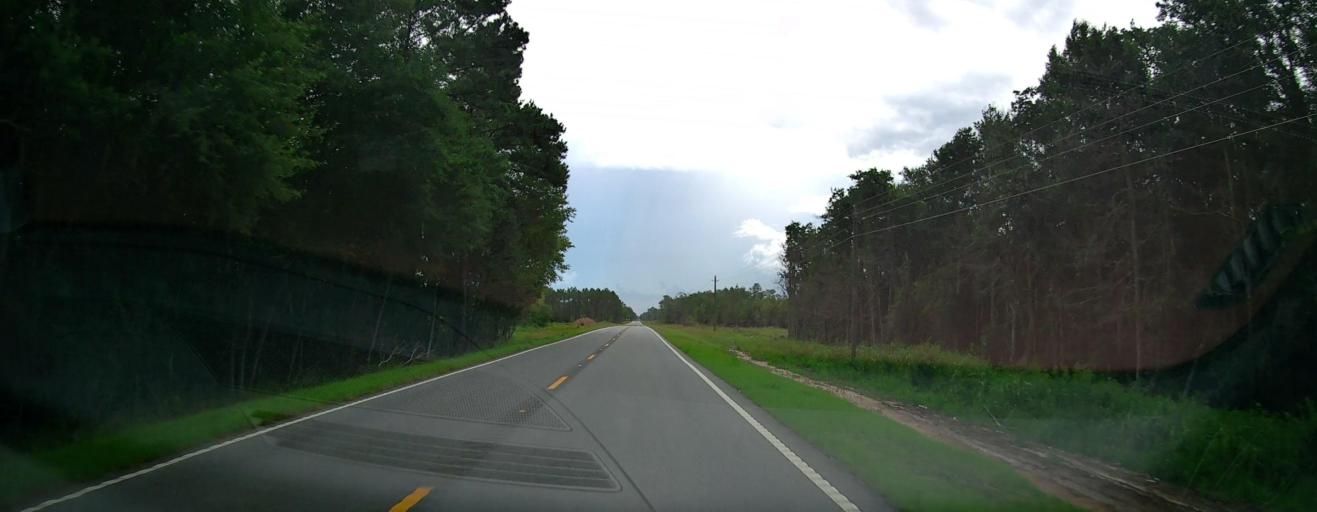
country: US
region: Georgia
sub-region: Pierce County
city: Blackshear
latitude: 31.3687
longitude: -82.0962
